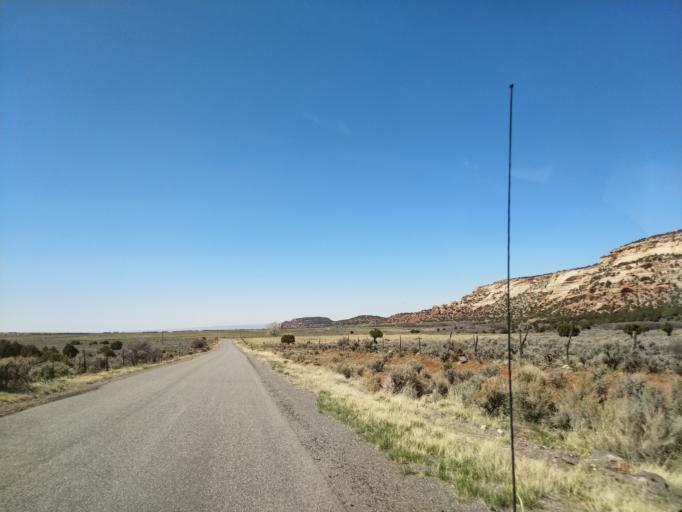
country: US
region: Colorado
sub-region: Mesa County
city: Loma
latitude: 38.9551
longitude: -109.0243
